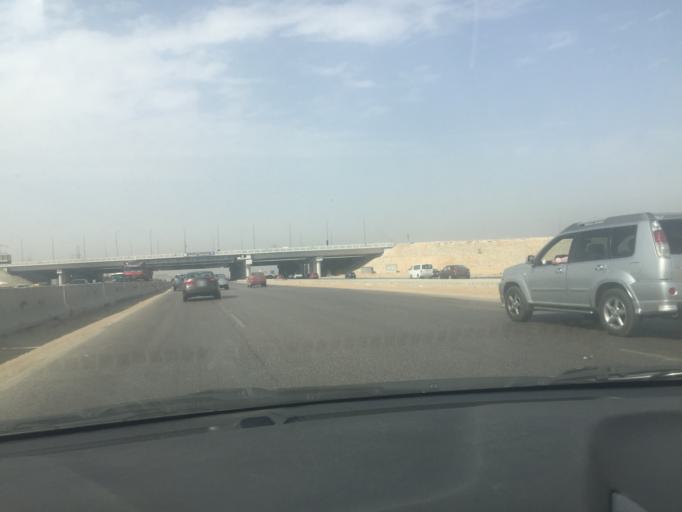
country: EG
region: Muhafazat al Qalyubiyah
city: Al Khankah
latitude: 30.0800
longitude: 31.4386
